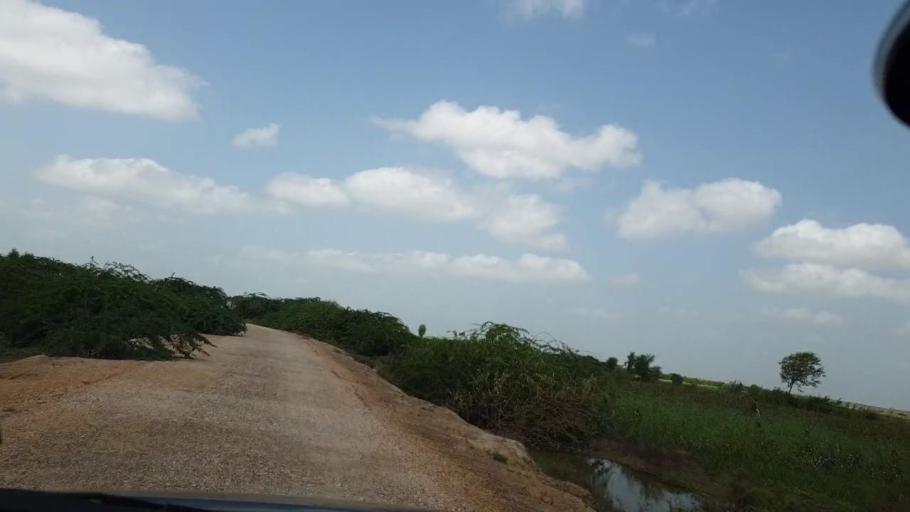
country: PK
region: Sindh
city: Kadhan
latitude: 24.5843
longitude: 69.1544
